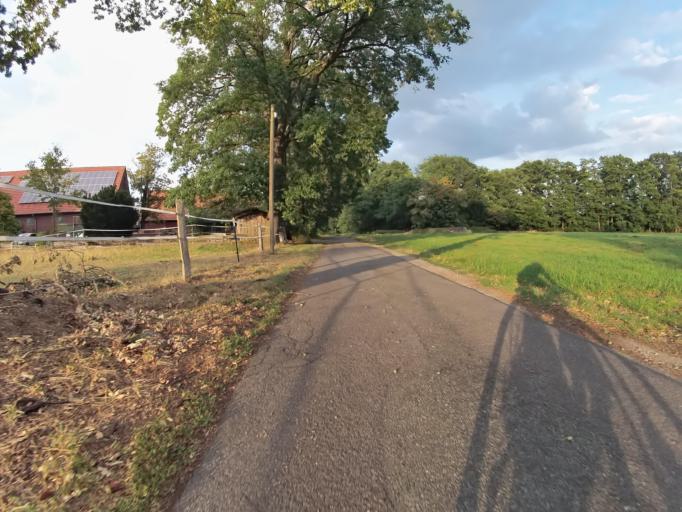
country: DE
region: North Rhine-Westphalia
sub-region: Regierungsbezirk Munster
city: Westerkappeln
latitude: 52.3581
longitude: 7.8991
